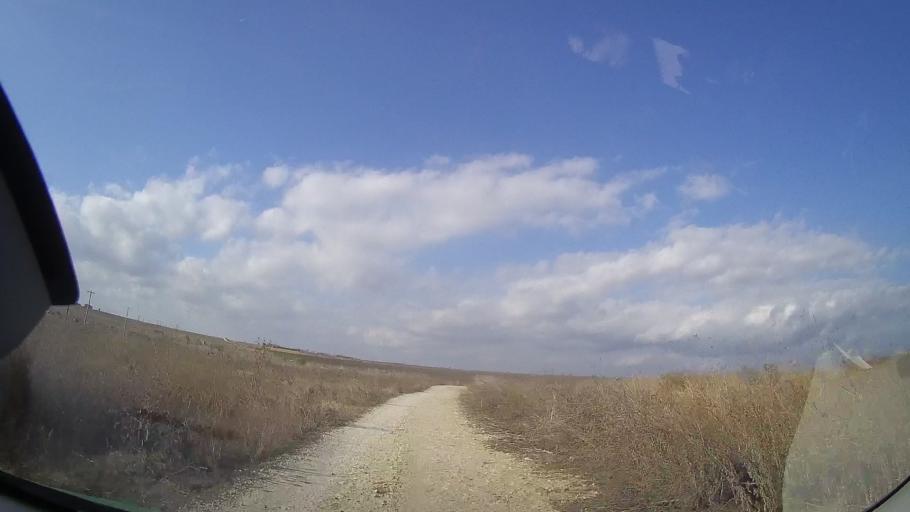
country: RO
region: Constanta
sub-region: Comuna Douazeci si Trei August
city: Douazeci si Trei August
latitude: 43.9086
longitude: 28.6089
